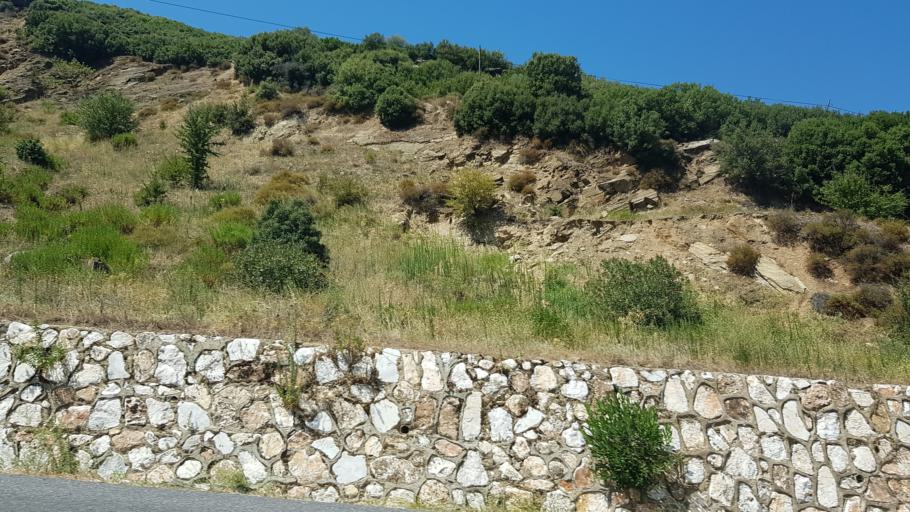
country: TR
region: Aydin
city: Akcaova
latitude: 37.5044
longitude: 28.1029
